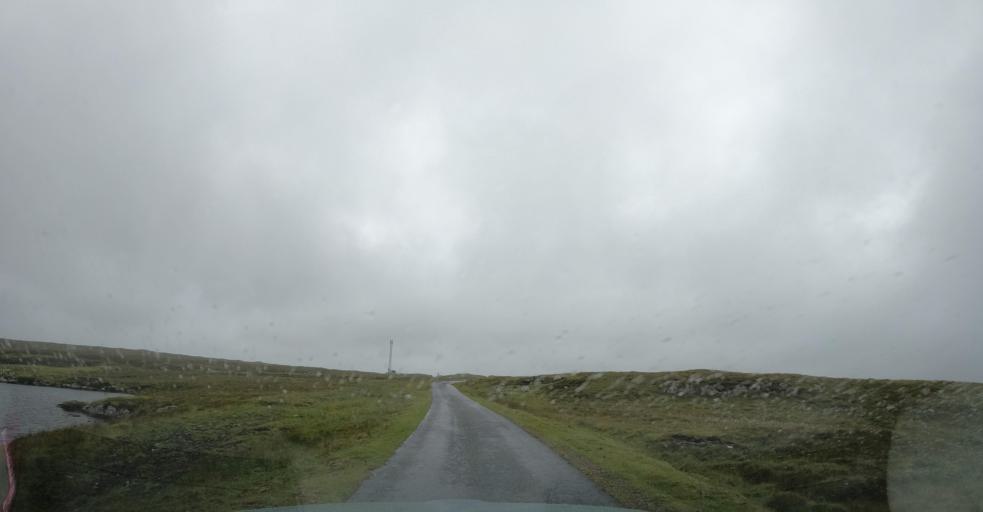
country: GB
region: Scotland
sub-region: Eilean Siar
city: Benbecula
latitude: 57.4937
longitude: -7.2281
